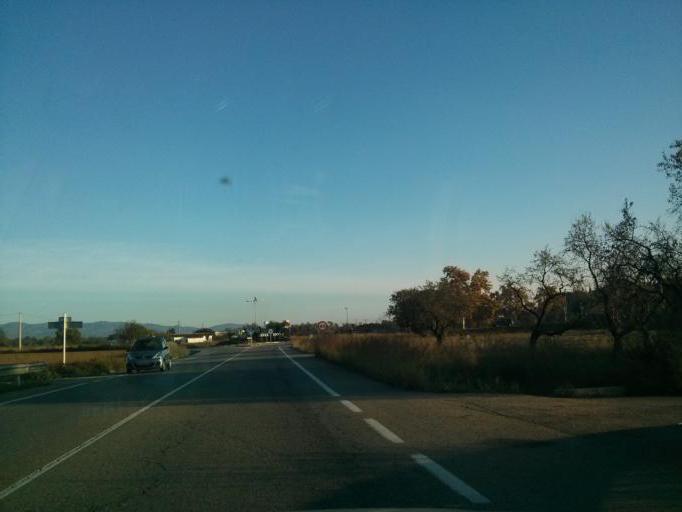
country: ES
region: Catalonia
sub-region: Provincia de Tarragona
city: Santa Oliva
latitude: 41.2506
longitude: 1.5444
